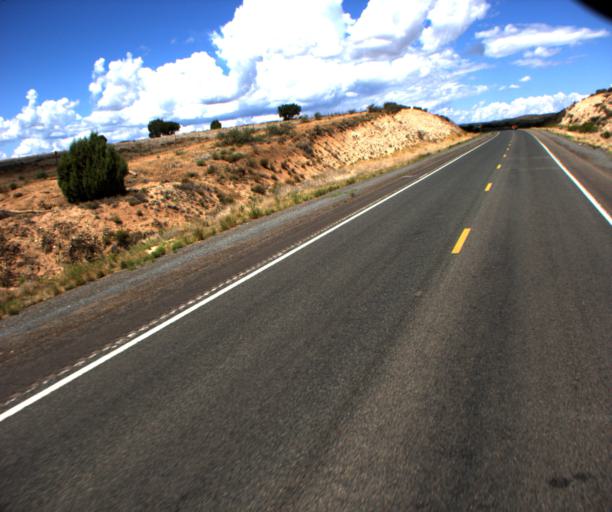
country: US
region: Arizona
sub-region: Yavapai County
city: Dewey-Humboldt
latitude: 34.5209
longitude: -112.0654
